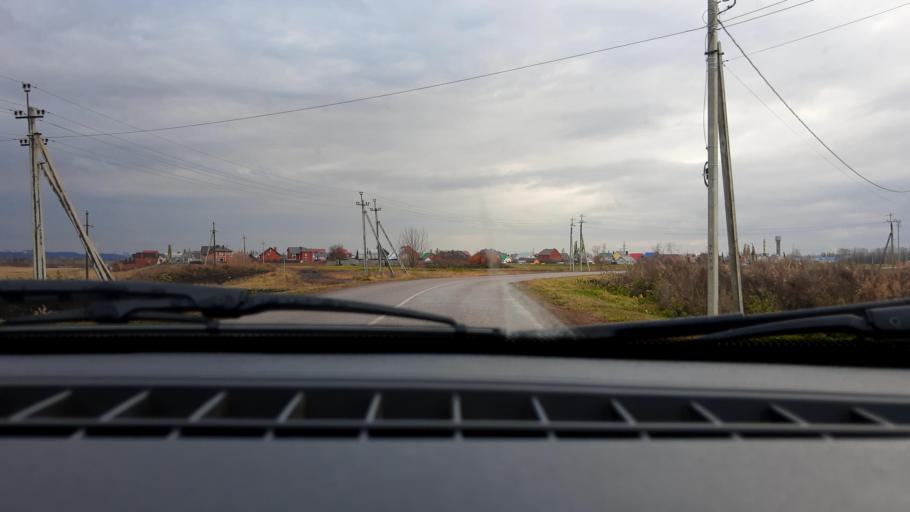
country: RU
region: Bashkortostan
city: Ufa
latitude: 54.8481
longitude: 56.0099
